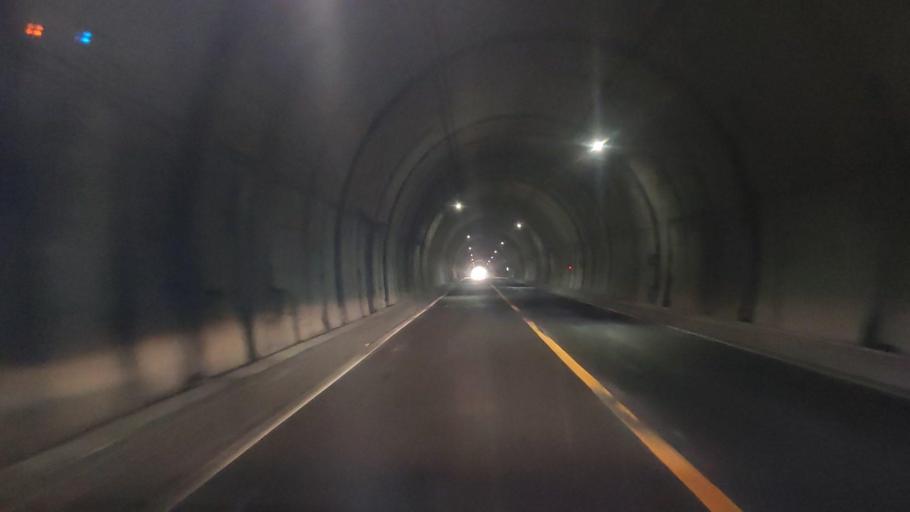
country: JP
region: Oita
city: Saiki
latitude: 32.8816
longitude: 131.9474
